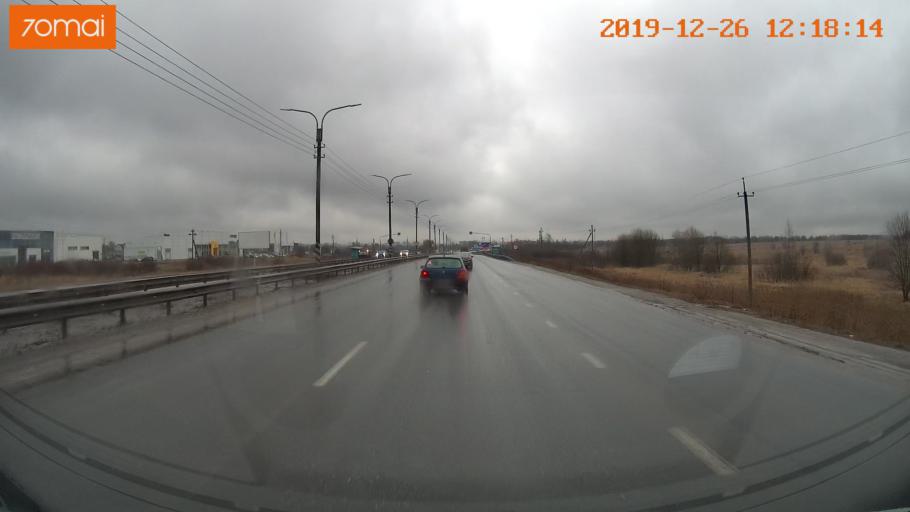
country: RU
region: Vologda
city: Tonshalovo
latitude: 59.1806
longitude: 37.9431
